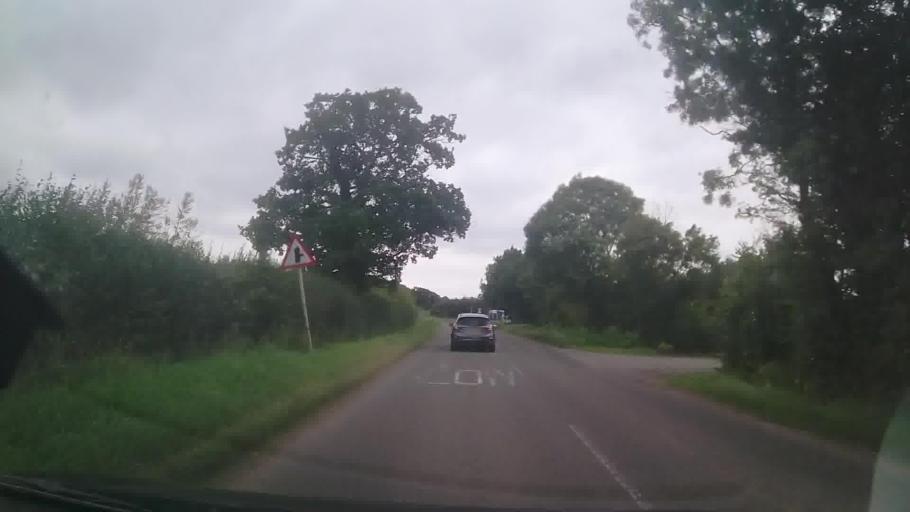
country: GB
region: England
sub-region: Leicestershire
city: Desford
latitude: 52.6585
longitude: -1.2914
